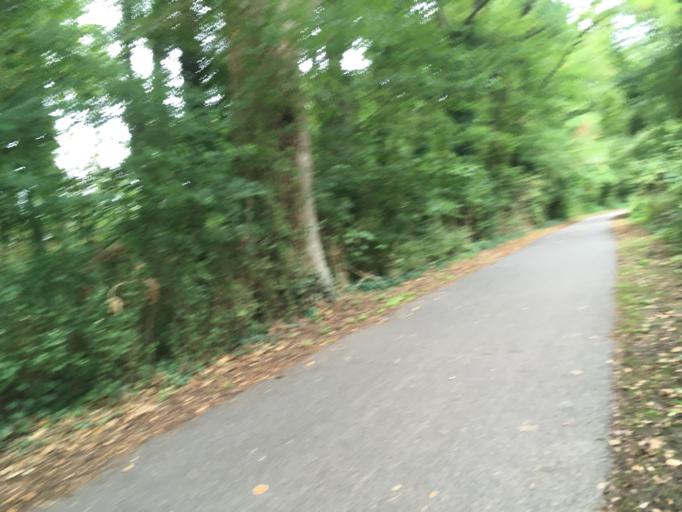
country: DE
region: Brandenburg
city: Prenzlau
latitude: 53.2955
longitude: 13.8671
